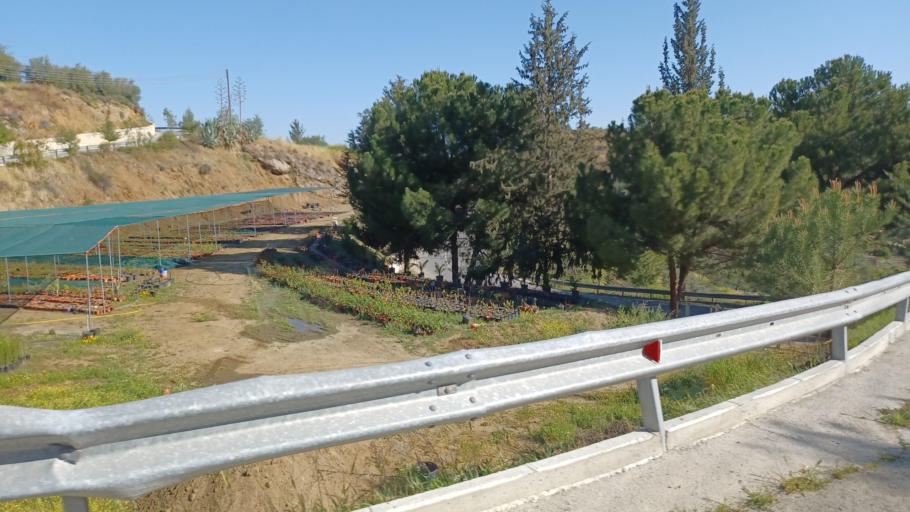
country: CY
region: Lefkosia
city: Peristerona
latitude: 35.0279
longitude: 33.0401
